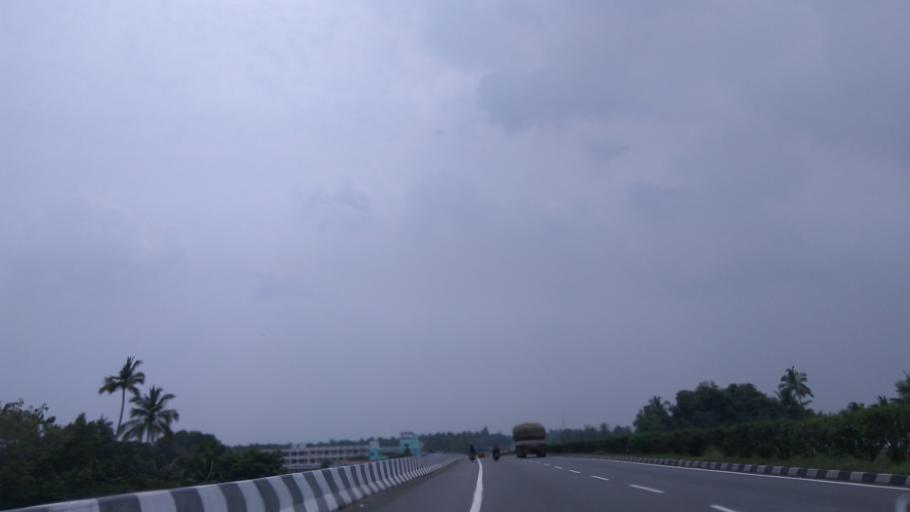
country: IN
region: Tamil Nadu
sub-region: Dharmapuri
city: Dharmapuri
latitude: 12.2447
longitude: 78.1951
